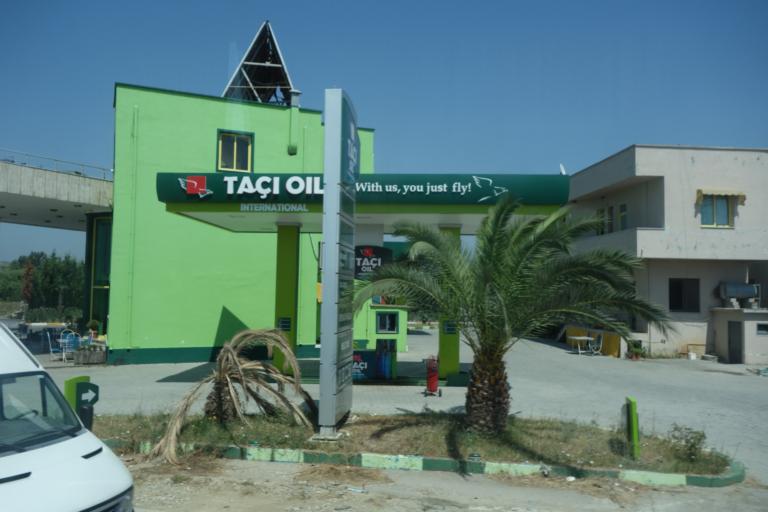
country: AL
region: Tirane
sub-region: Rrethi i Tiranes
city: Shengjergj
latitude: 41.2034
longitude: 19.5357
